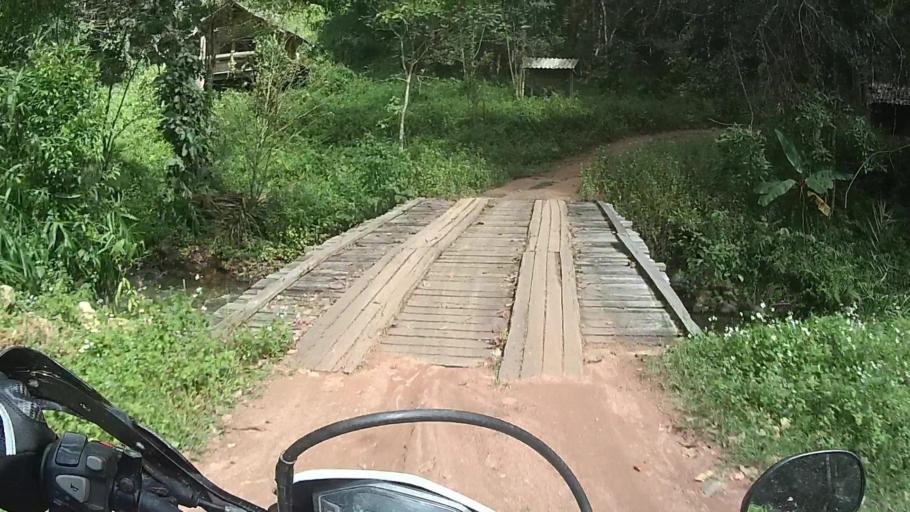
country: TH
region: Lampang
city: Mueang Pan
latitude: 18.9701
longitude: 99.4245
